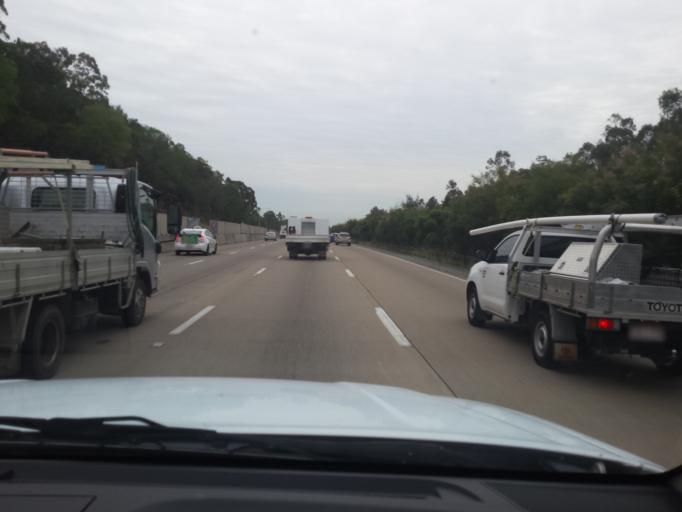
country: AU
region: Queensland
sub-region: Gold Coast
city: Oxenford
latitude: -27.8504
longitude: 153.3069
